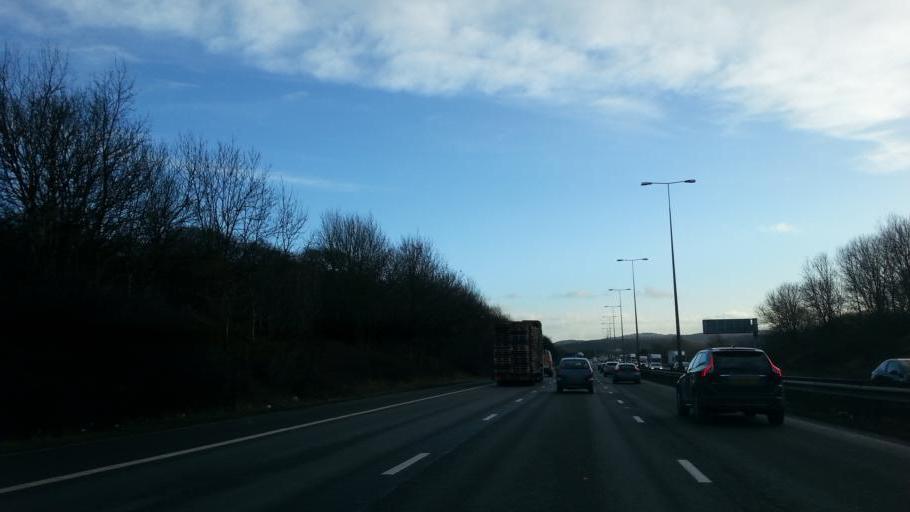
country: GB
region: England
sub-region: Leicestershire
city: Shepshed
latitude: 52.7882
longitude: -1.2868
